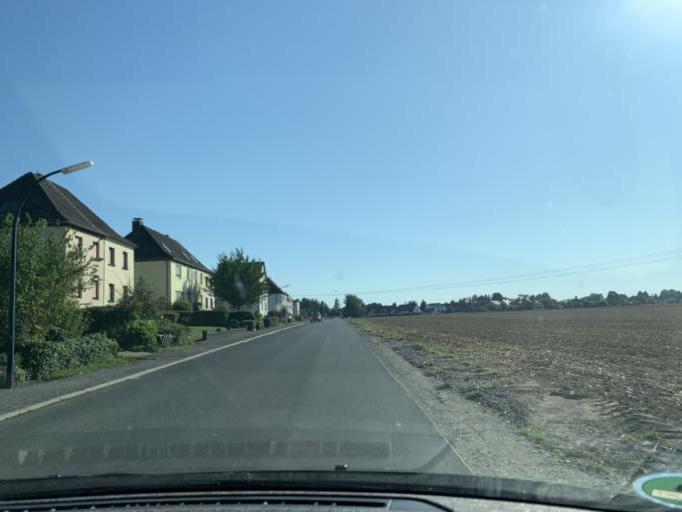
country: DE
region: North Rhine-Westphalia
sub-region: Regierungsbezirk Arnsberg
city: Holzwickede
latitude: 51.4830
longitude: 7.6114
